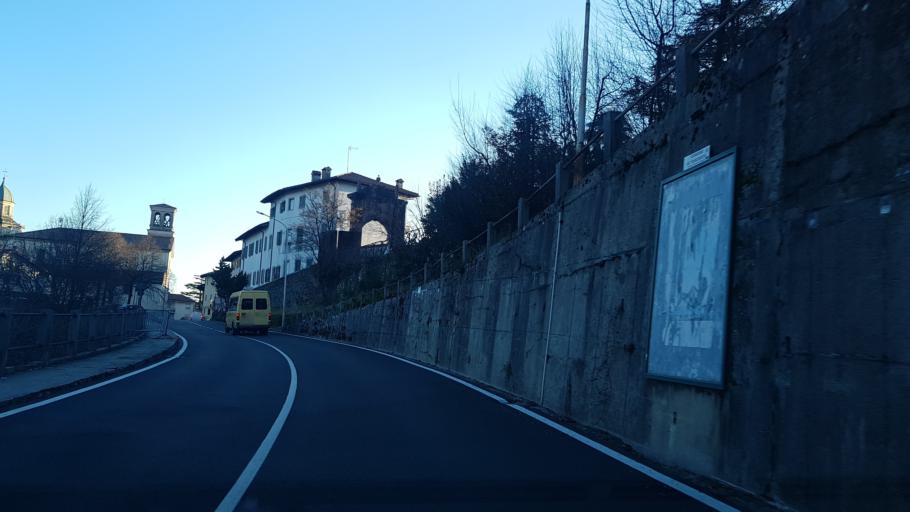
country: IT
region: Friuli Venezia Giulia
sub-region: Provincia di Udine
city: Tarcento
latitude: 46.2175
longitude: 13.2214
